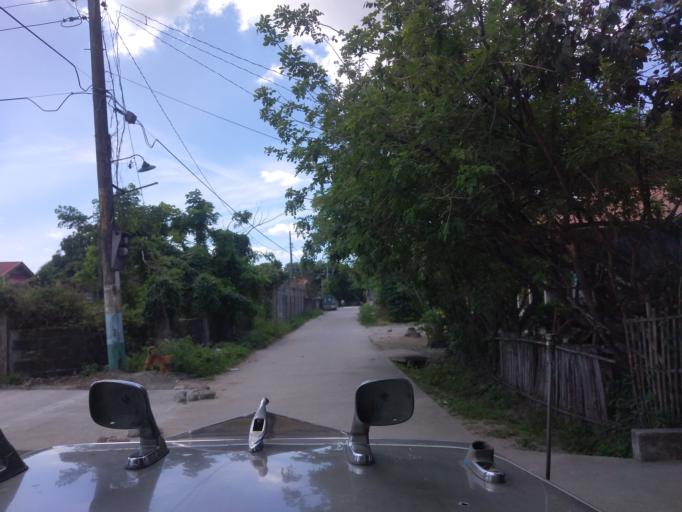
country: PH
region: Central Luzon
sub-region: Province of Pampanga
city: Santa Rita
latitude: 15.0080
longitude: 120.5944
